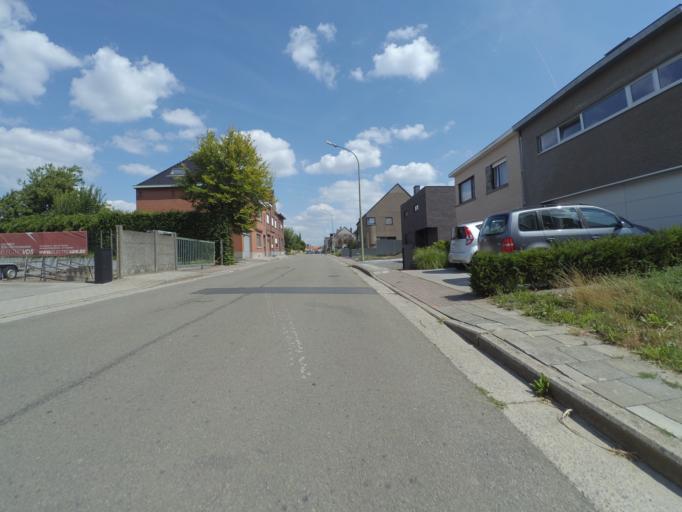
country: BE
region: Flanders
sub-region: Provincie Oost-Vlaanderen
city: Zottegem
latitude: 50.8635
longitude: 3.7985
